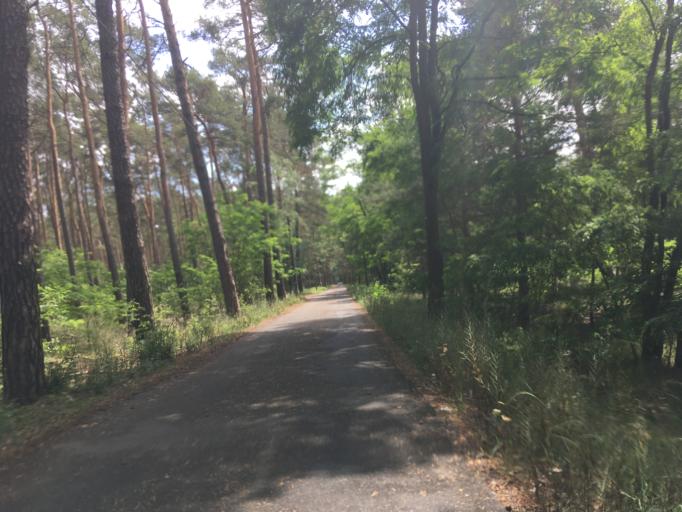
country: DE
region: Berlin
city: Muggelheim
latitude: 52.4004
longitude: 13.6497
